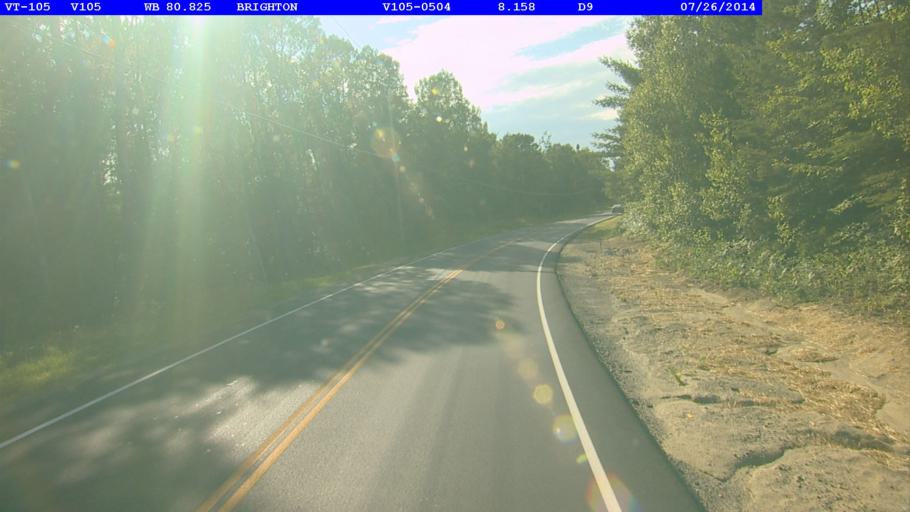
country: US
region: New Hampshire
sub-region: Coos County
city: Stratford
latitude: 44.7872
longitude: -71.8244
